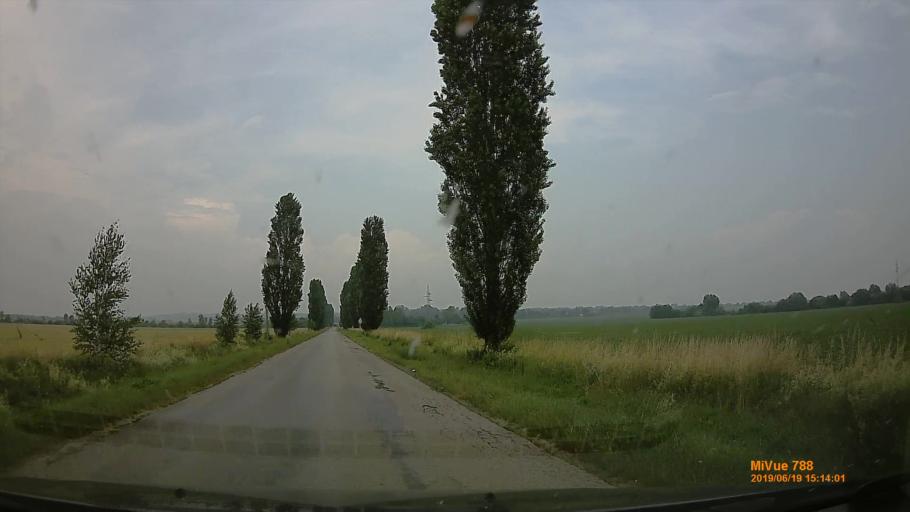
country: HU
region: Baranya
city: Szigetvar
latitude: 46.0651
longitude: 17.8208
